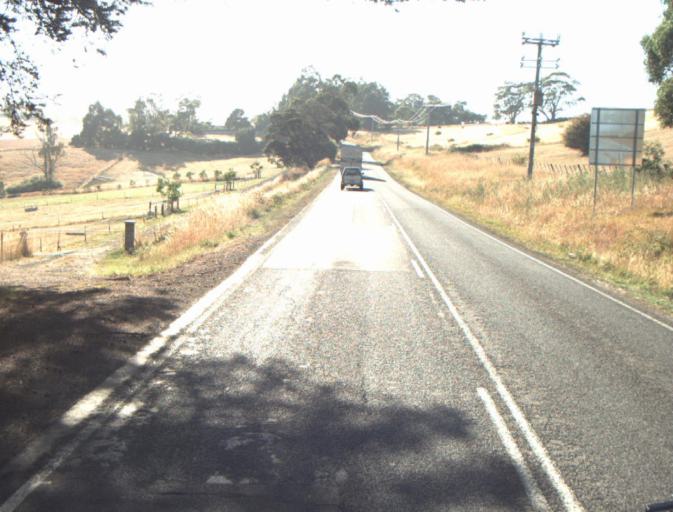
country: AU
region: Tasmania
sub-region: Launceston
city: Newstead
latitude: -41.4451
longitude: 147.2159
